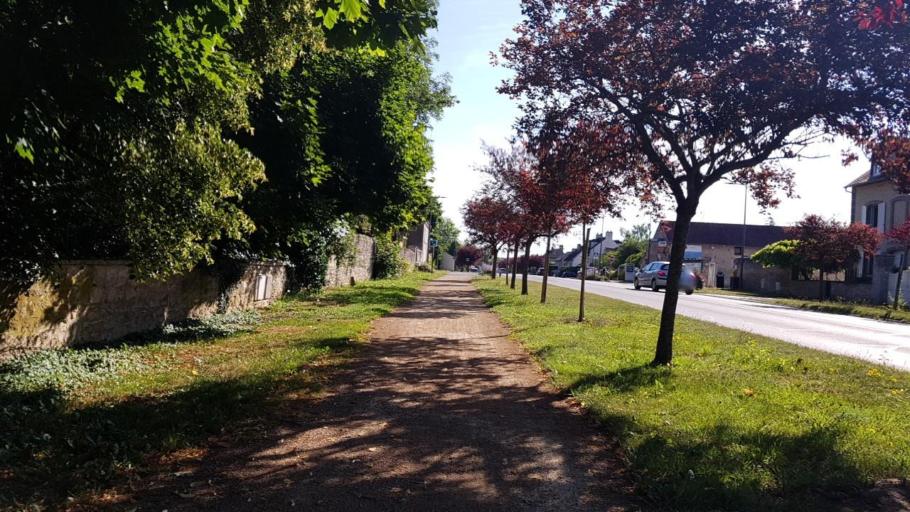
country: FR
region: Picardie
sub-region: Departement de l'Oise
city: Chamant
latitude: 49.2211
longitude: 2.6070
